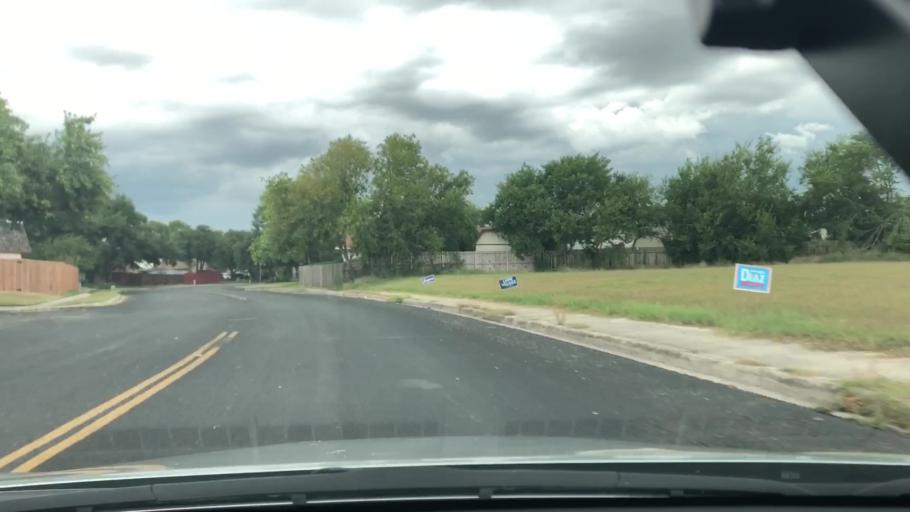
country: US
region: Texas
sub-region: Bexar County
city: Kirby
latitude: 29.4769
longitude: -98.3578
